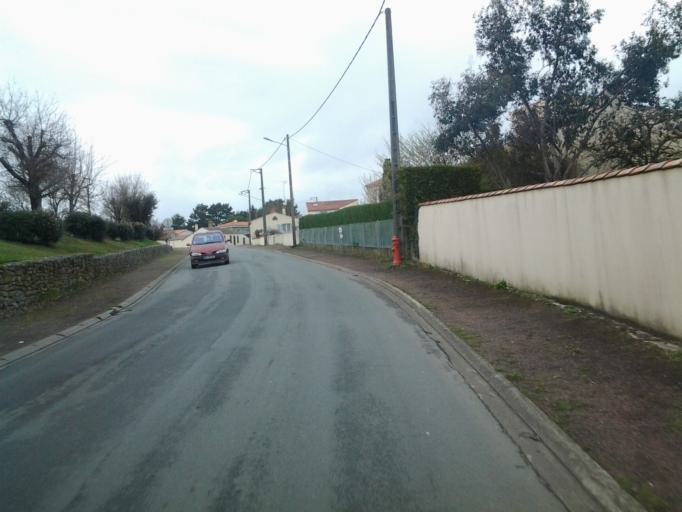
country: FR
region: Pays de la Loire
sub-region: Departement de la Vendee
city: Avrille
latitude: 46.4665
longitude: -1.4903
